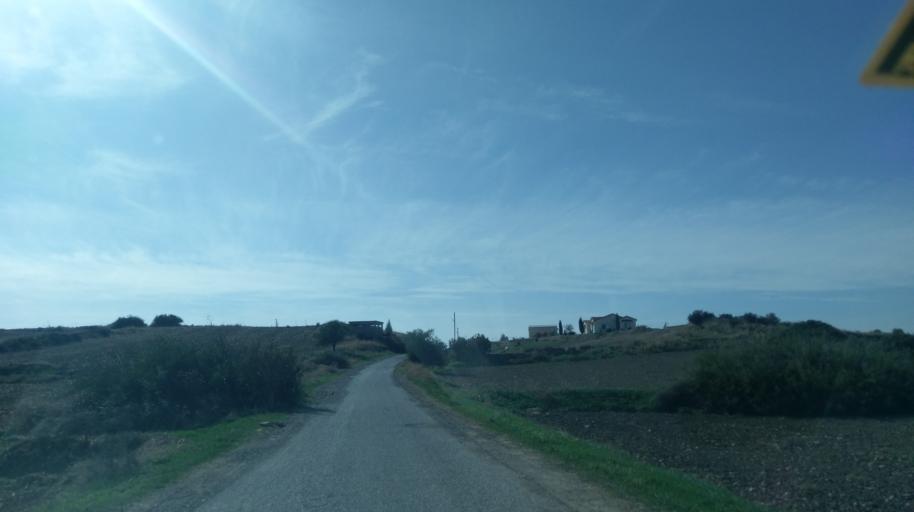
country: CY
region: Ammochostos
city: Trikomo
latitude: 35.3629
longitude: 33.9280
